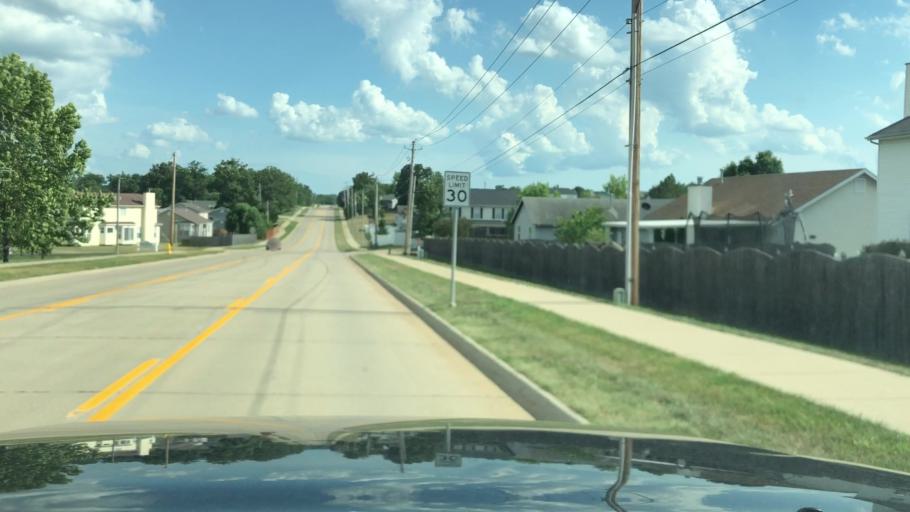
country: US
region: Missouri
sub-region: Saint Charles County
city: Wentzville
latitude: 38.8350
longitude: -90.8922
